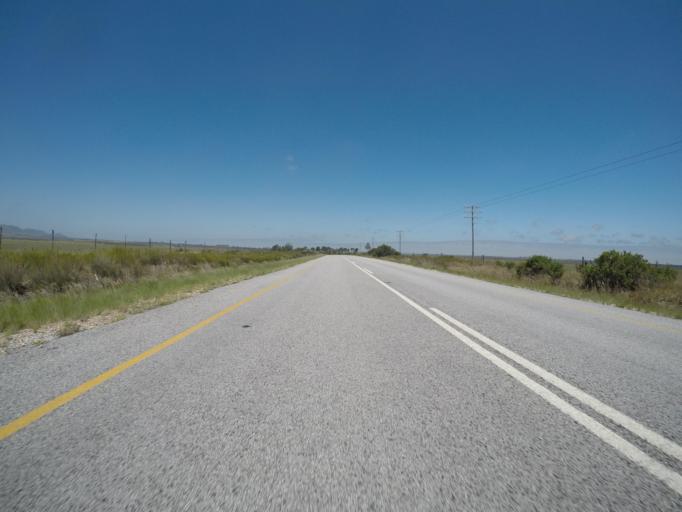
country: ZA
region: Eastern Cape
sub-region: Cacadu District Municipality
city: Kruisfontein
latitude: -34.0158
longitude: 24.5684
